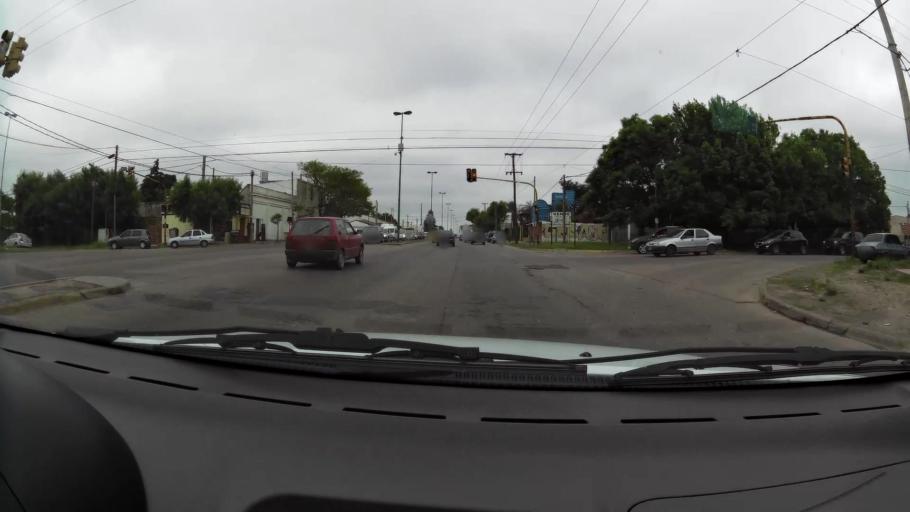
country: AR
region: Buenos Aires
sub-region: Partido de La Plata
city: La Plata
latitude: -34.9506
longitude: -57.9989
